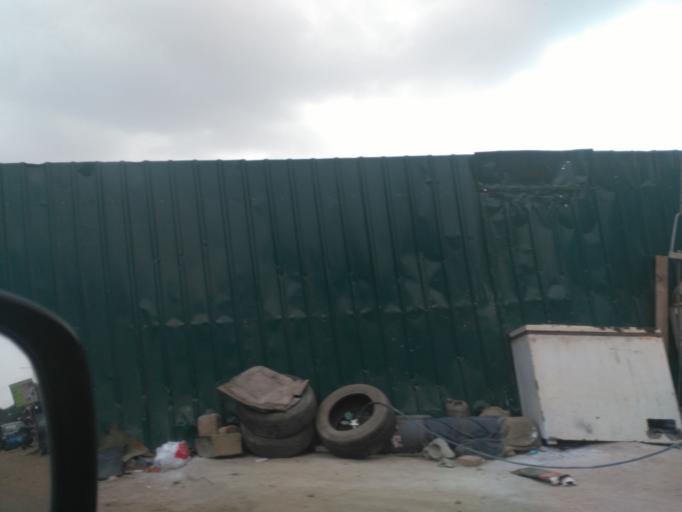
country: GH
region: Greater Accra
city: Accra
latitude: 5.5979
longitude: -0.1813
